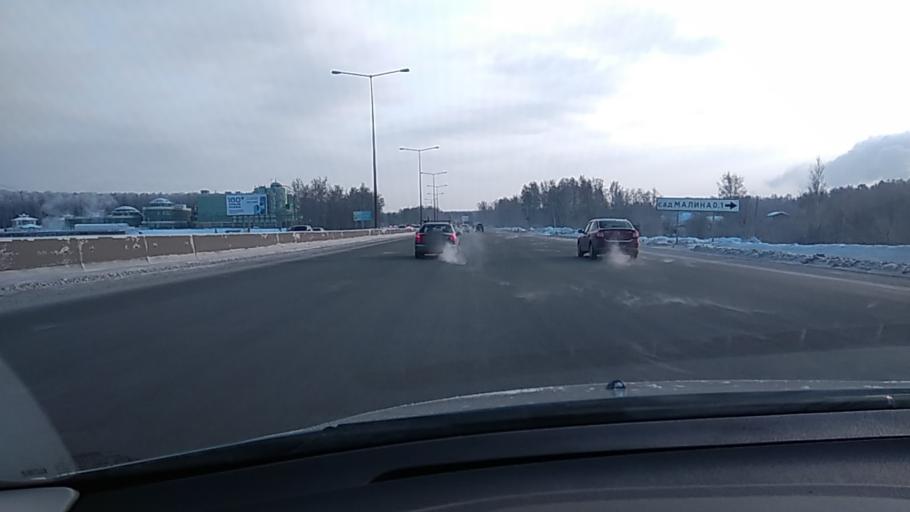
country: RU
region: Sverdlovsk
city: Istok
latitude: 56.7778
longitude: 60.7108
